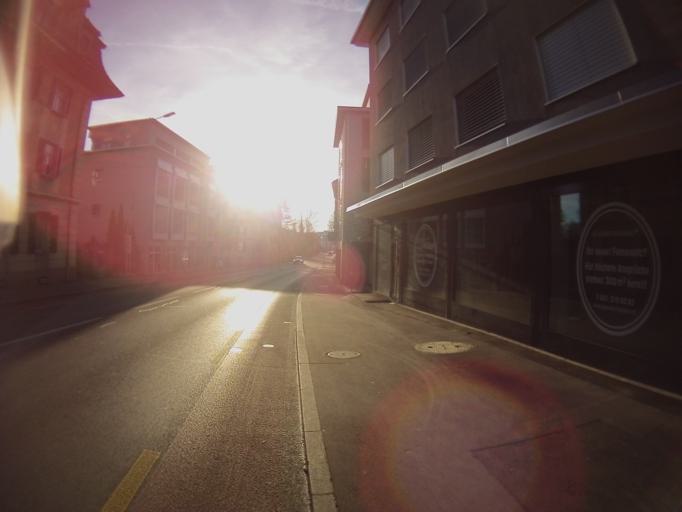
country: CH
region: Zug
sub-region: Zug
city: Cham
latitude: 47.1793
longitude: 8.4579
